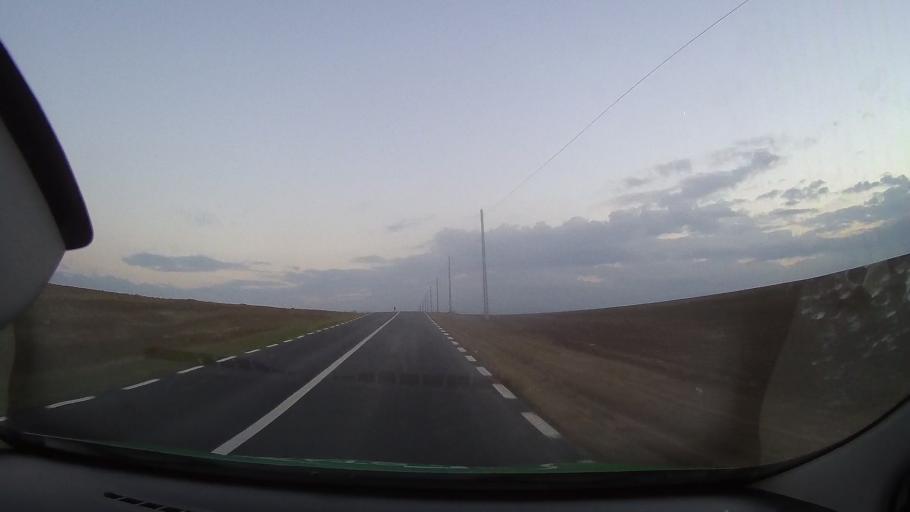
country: RO
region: Constanta
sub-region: Comuna Oltina
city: Oltina
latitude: 44.1359
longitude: 27.6665
